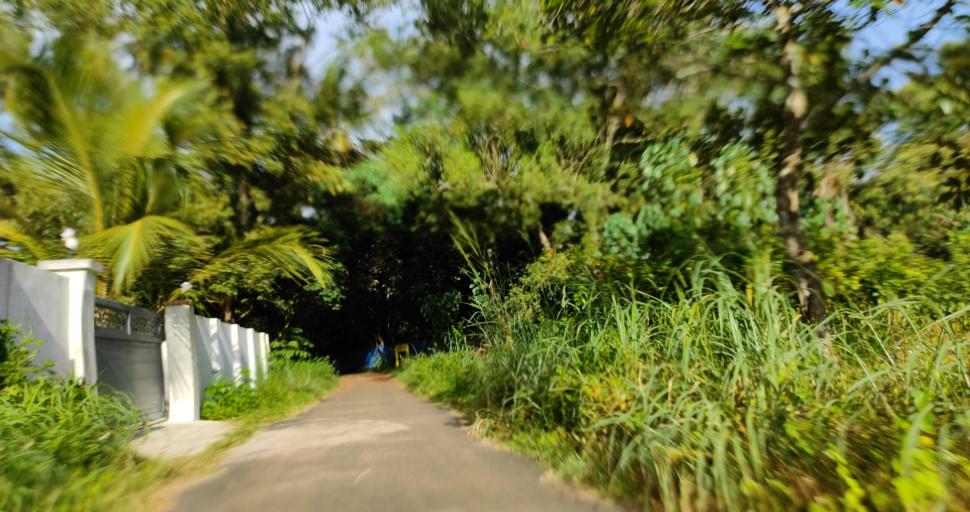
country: IN
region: Kerala
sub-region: Alappuzha
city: Shertallai
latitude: 9.6226
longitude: 76.3336
